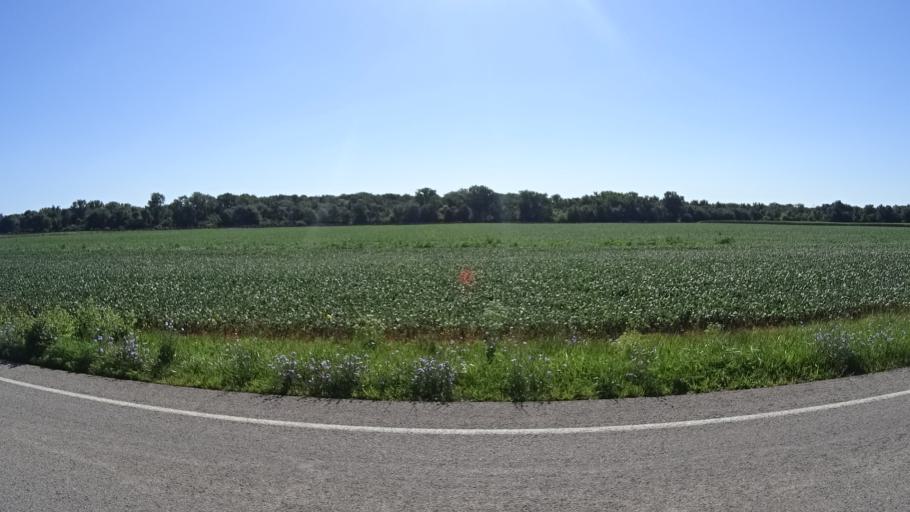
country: US
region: Ohio
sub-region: Erie County
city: Sandusky
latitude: 41.3752
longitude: -82.7244
